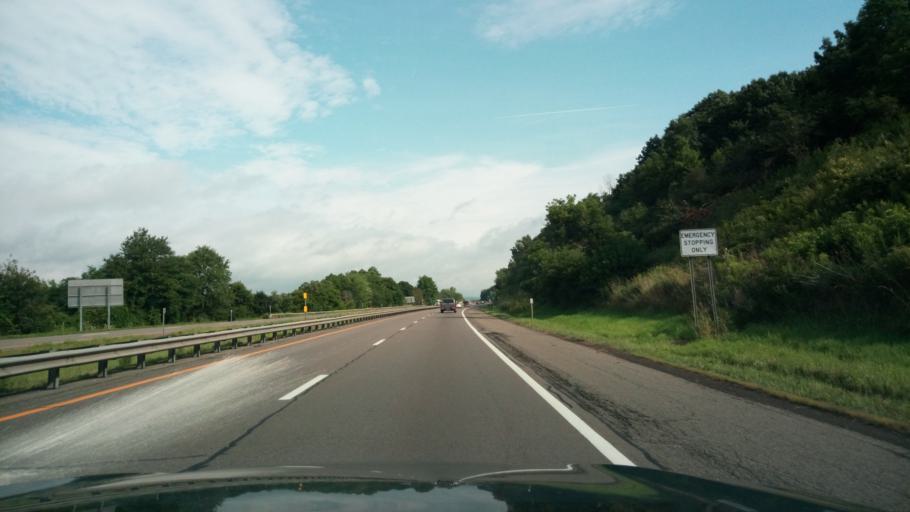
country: US
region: New York
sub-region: Chemung County
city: Elmira
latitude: 42.1057
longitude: -76.7942
